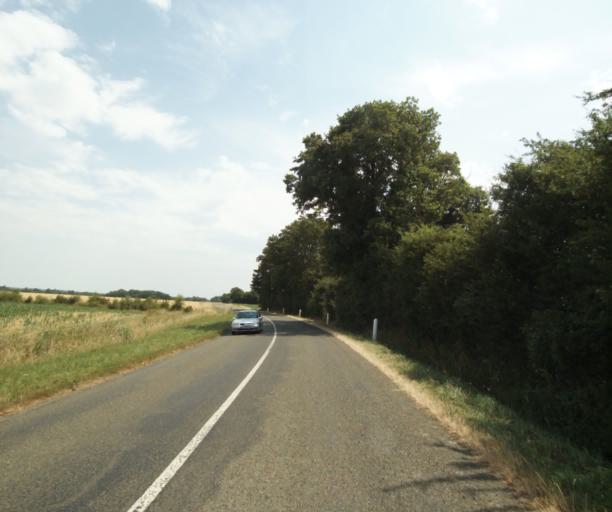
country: FR
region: Centre
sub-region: Departement d'Eure-et-Loir
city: La Bazoche-Gouet
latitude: 48.1778
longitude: 1.0257
